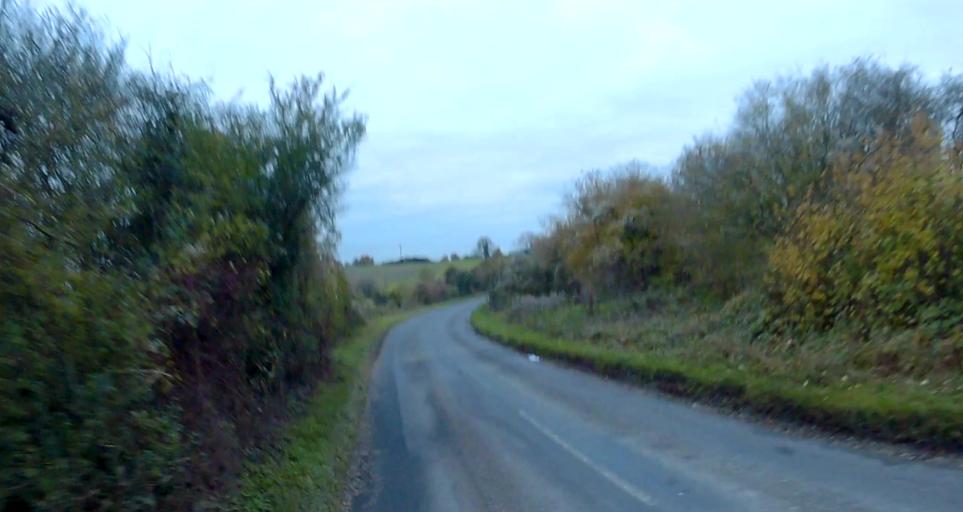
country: GB
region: England
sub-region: Hampshire
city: Odiham
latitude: 51.2479
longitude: -0.9690
